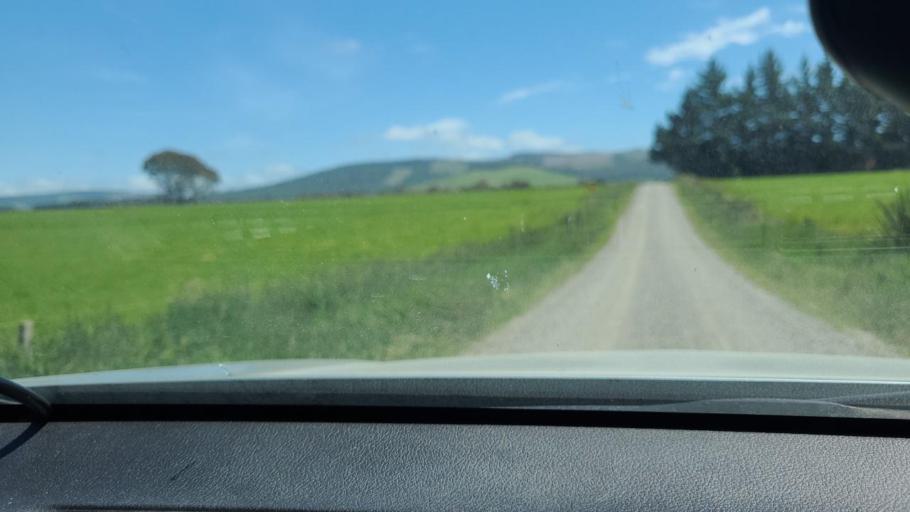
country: NZ
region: Southland
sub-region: Southland District
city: Riverton
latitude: -46.0361
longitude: 168.0052
